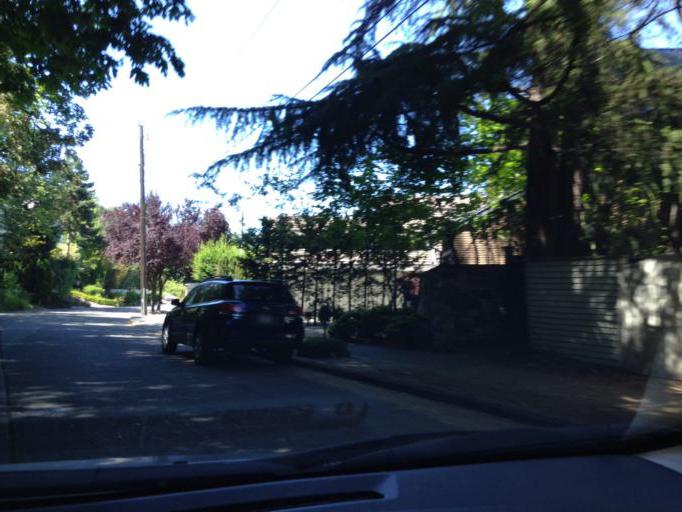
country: US
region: Washington
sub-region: King County
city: Seattle
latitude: 47.5922
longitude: -122.2875
